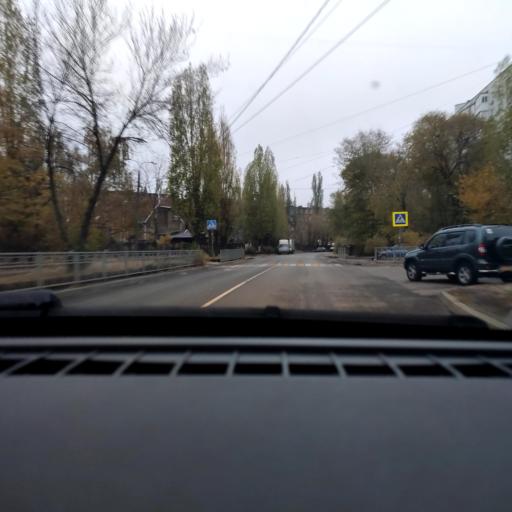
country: RU
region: Voronezj
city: Voronezh
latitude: 51.6495
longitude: 39.1443
